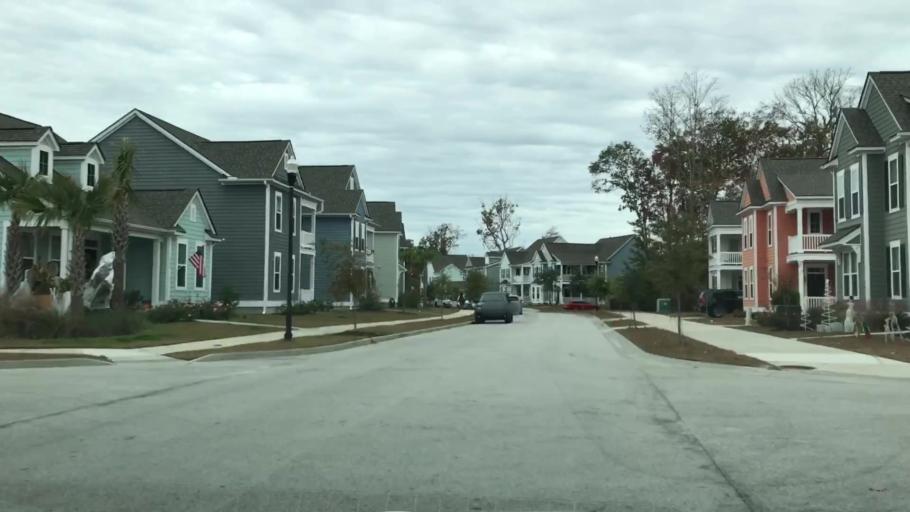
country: US
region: South Carolina
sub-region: Charleston County
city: Shell Point
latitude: 32.8086
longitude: -80.0697
